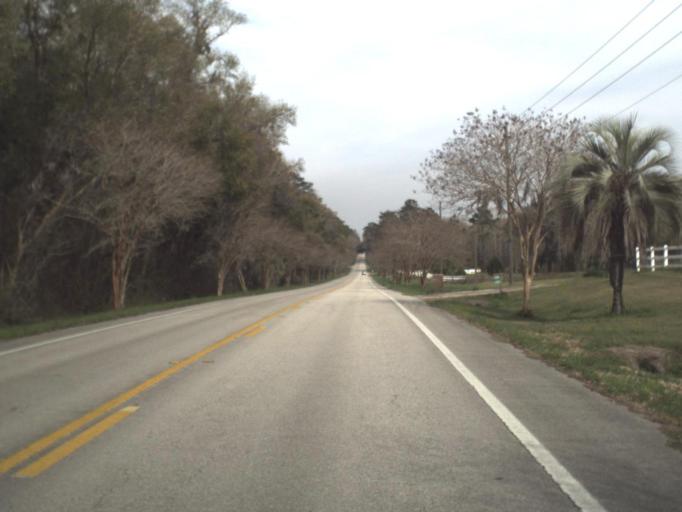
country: US
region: Florida
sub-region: Jefferson County
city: Monticello
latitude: 30.5320
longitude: -83.9573
